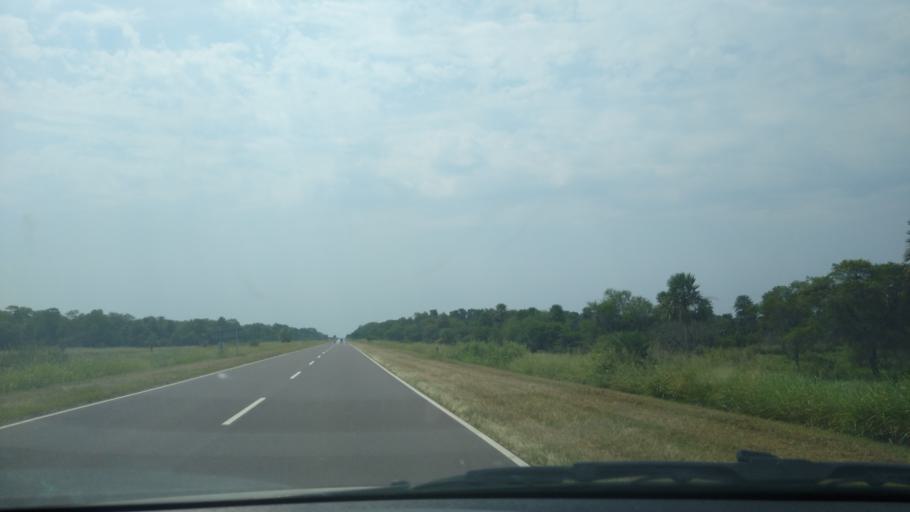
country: AR
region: Chaco
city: La Eduvigis
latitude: -27.0186
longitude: -58.9686
